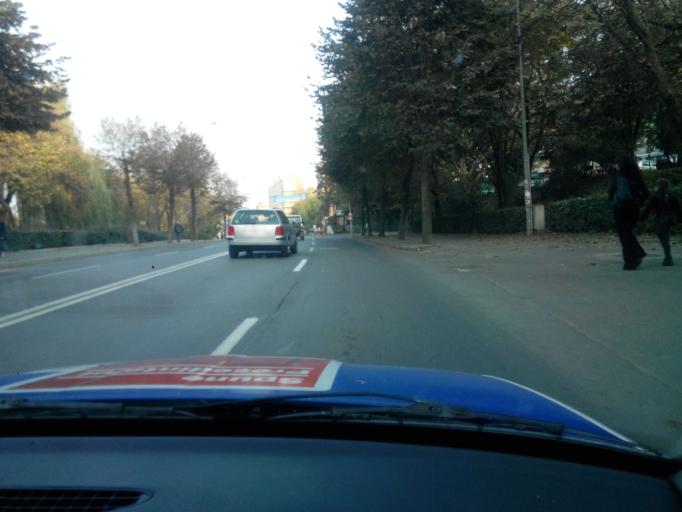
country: RO
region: Tulcea
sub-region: Municipiul Tulcea
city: Tulcea
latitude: 45.1794
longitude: 28.7845
